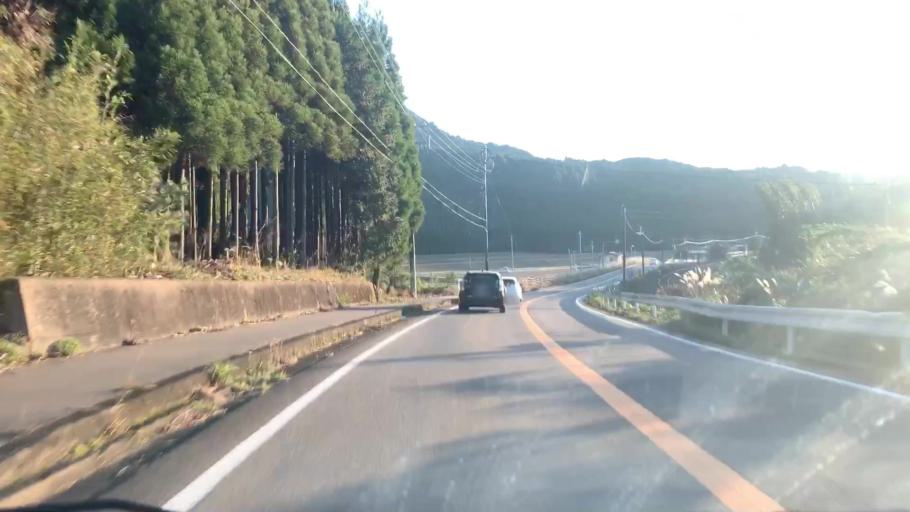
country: JP
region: Saga Prefecture
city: Karatsu
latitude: 33.3397
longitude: 129.9803
